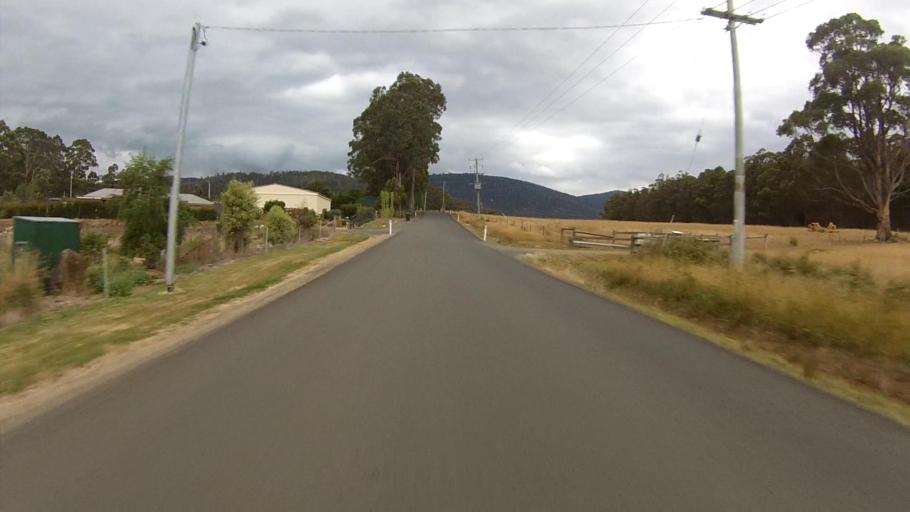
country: AU
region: Tasmania
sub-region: Huon Valley
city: Huonville
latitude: -42.9732
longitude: 147.0909
